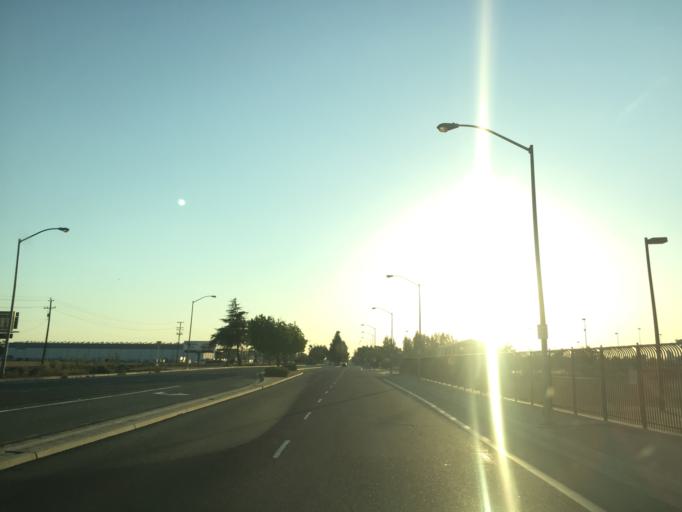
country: US
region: California
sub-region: Fresno County
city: Sunnyside
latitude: 36.7652
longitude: -119.7126
